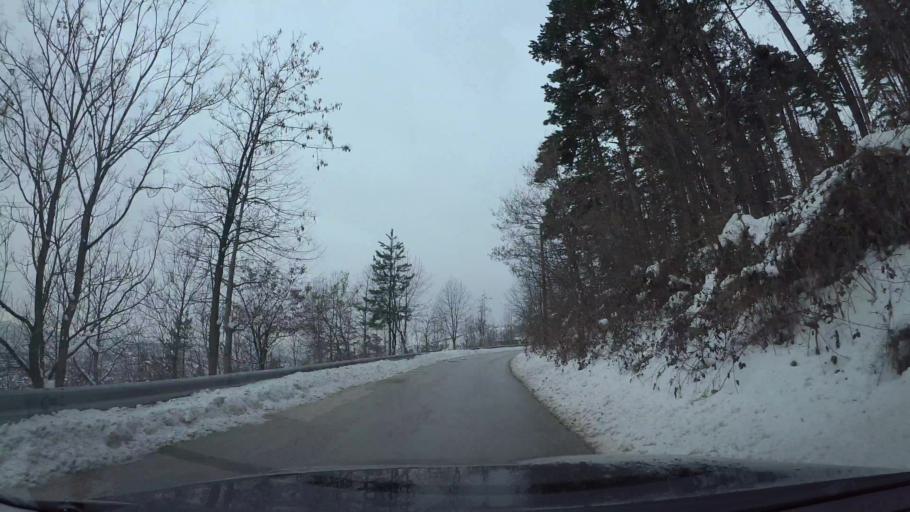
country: BA
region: Federation of Bosnia and Herzegovina
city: Kobilja Glava
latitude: 43.8654
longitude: 18.4431
